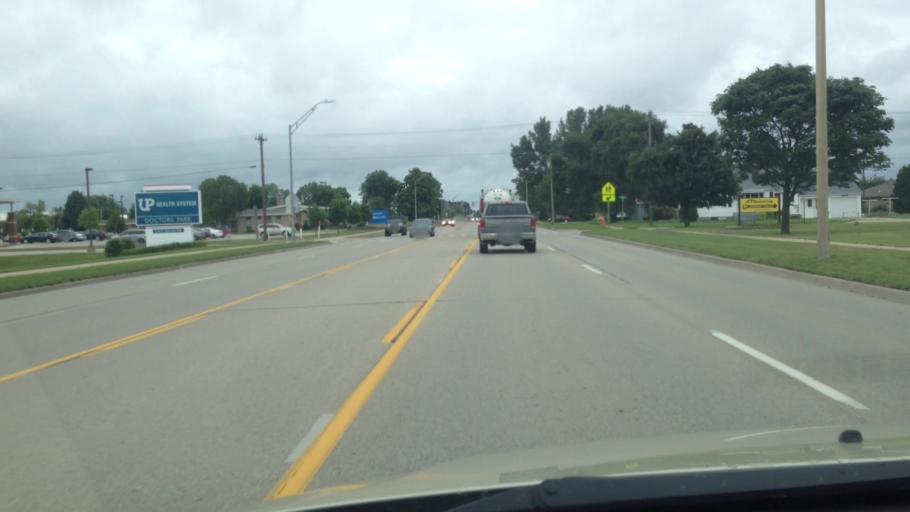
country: US
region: Michigan
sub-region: Delta County
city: Escanaba
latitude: 45.7365
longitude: -87.0799
